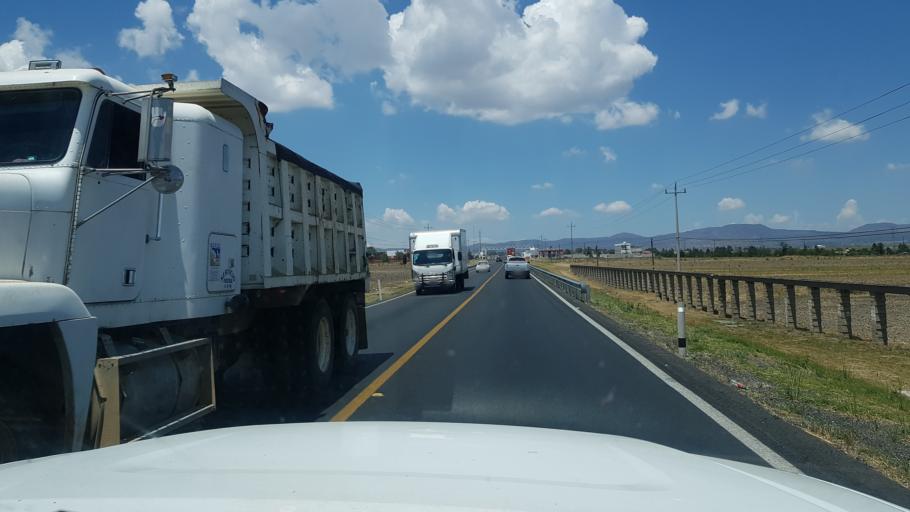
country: MX
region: Hidalgo
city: Calpulalpan
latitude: 19.5819
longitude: -98.5325
